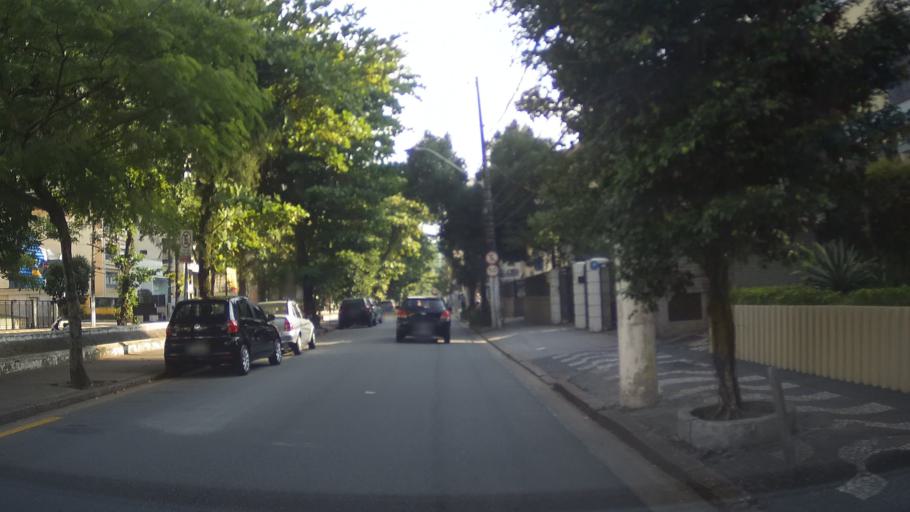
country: BR
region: Sao Paulo
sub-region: Santos
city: Santos
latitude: -23.9633
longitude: -46.3283
